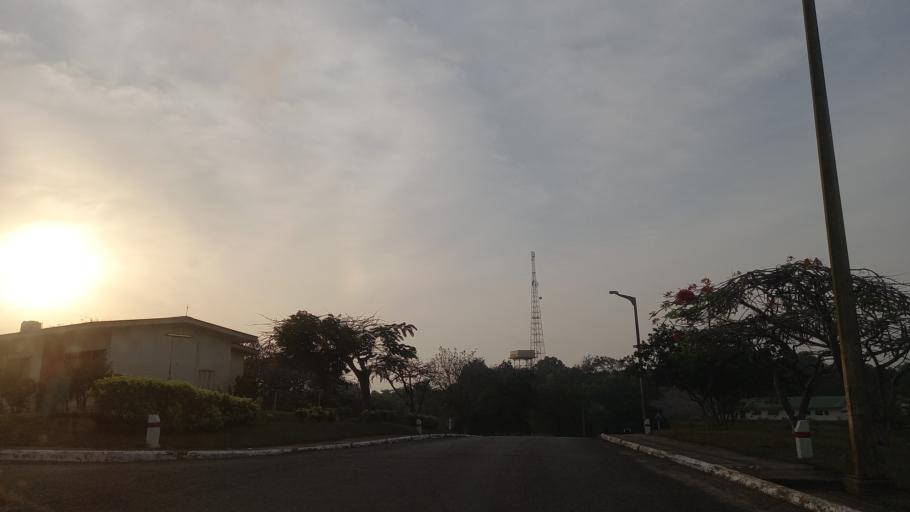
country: GH
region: Western
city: Shama Junction
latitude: 4.9801
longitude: -1.6588
